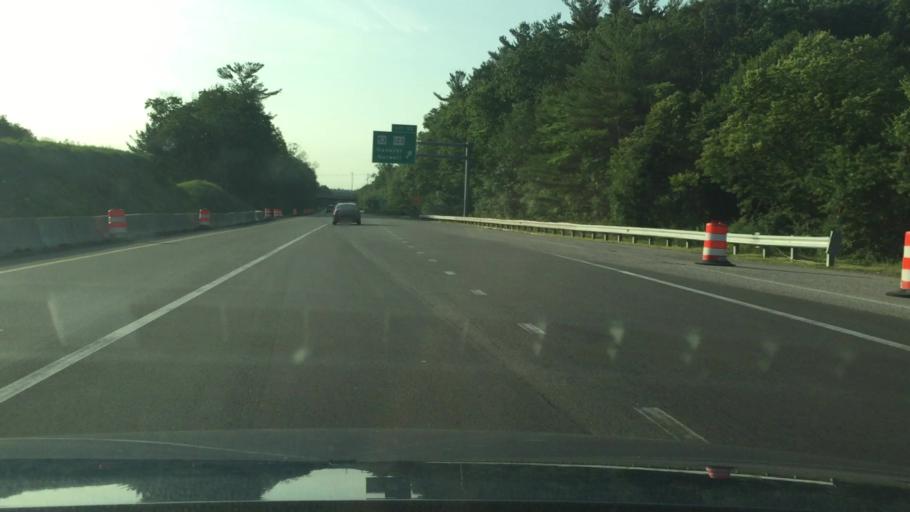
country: US
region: Massachusetts
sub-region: Plymouth County
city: Hanover
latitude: 42.1530
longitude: -70.8503
